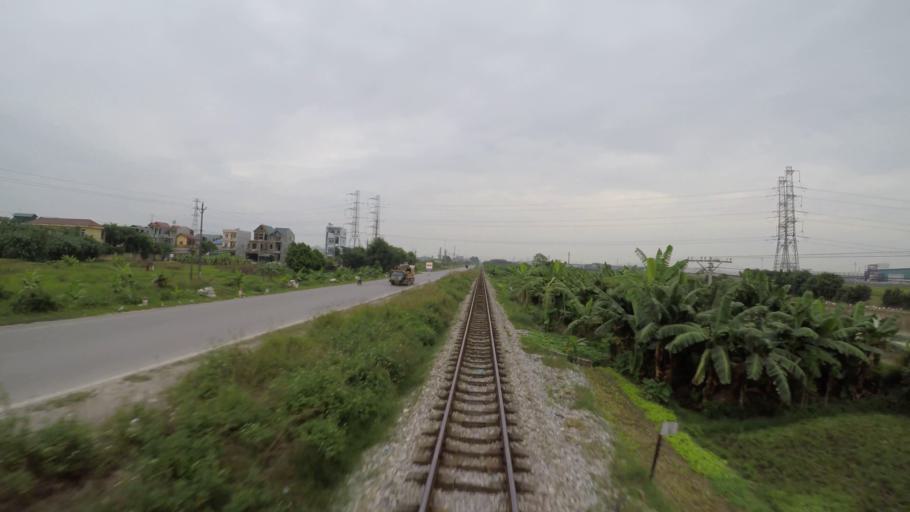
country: VN
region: Hung Yen
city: Ban Yen Nhan
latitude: 20.9855
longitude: 106.0410
